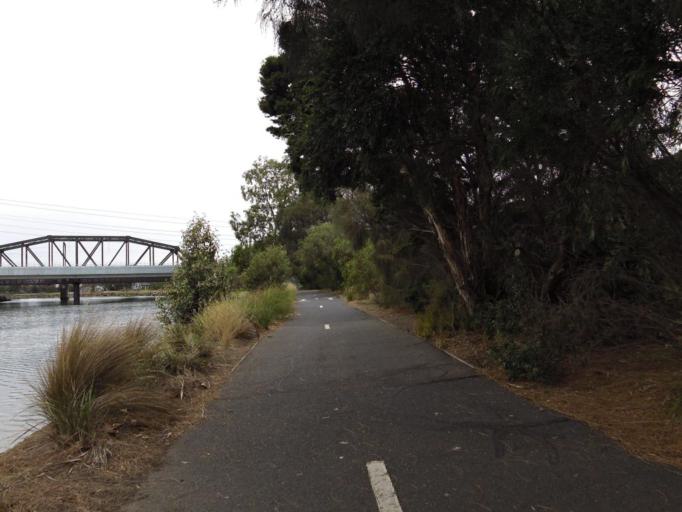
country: AU
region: Victoria
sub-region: Maribyrnong
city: Footscray
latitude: -37.7997
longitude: 144.9162
